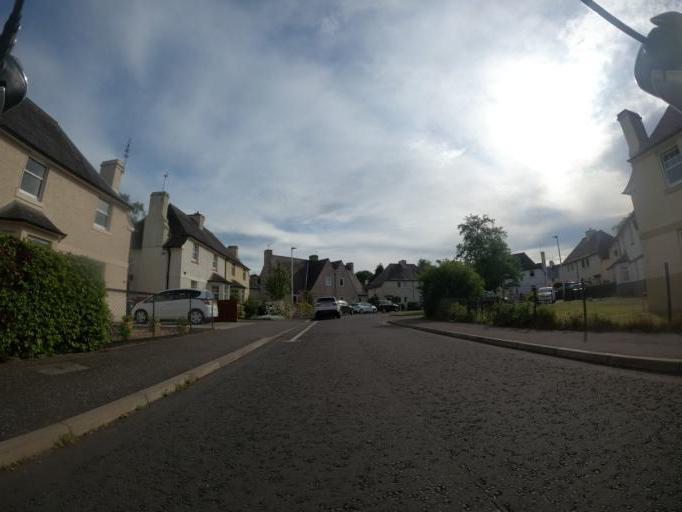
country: GB
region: Scotland
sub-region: Edinburgh
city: Edinburgh
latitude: 55.9730
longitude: -3.2214
